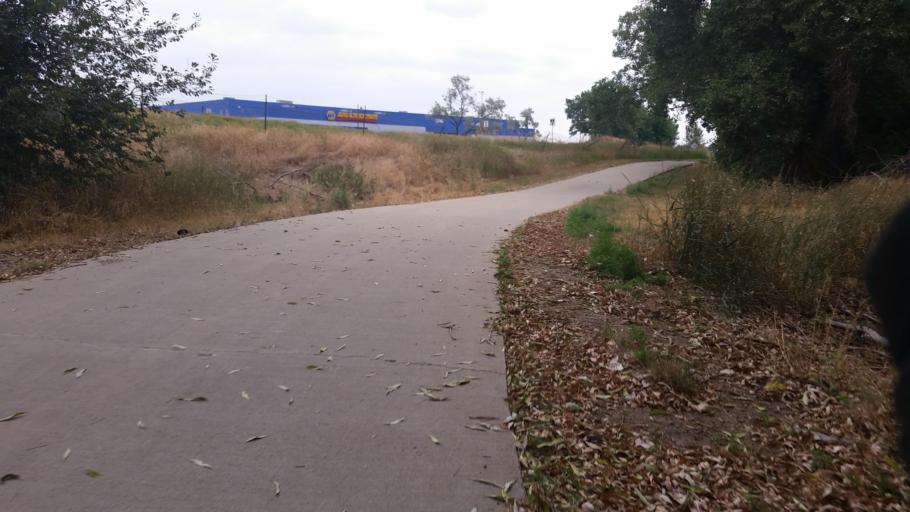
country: US
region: Colorado
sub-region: Adams County
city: Welby
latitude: 39.8276
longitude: -104.9632
